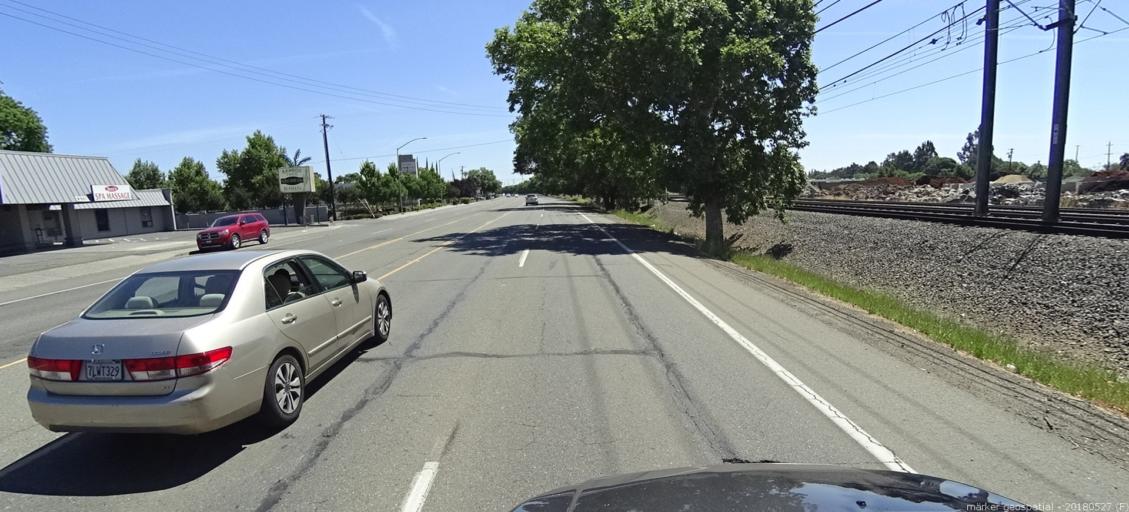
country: US
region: California
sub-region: Sacramento County
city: Rosemont
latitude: 38.5482
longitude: -121.3879
